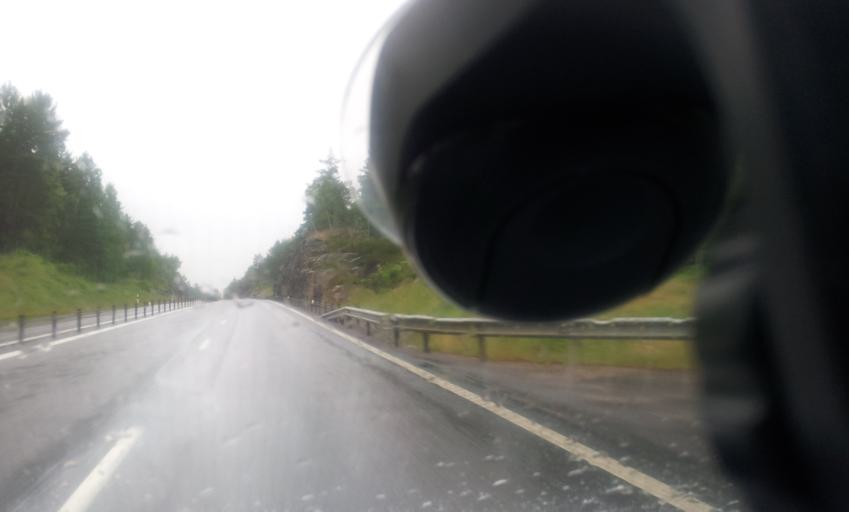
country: SE
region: OEstergoetland
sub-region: Valdemarsviks Kommun
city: Gusum
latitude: 58.3409
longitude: 16.4508
